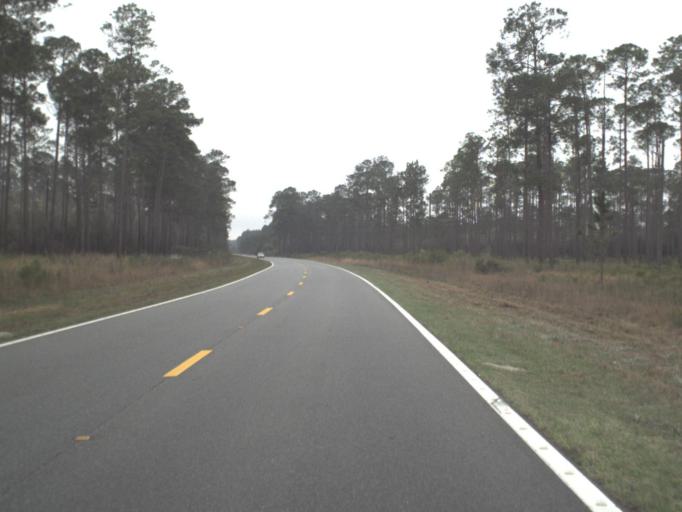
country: US
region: Florida
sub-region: Liberty County
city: Bristol
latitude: 30.3114
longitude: -84.8295
